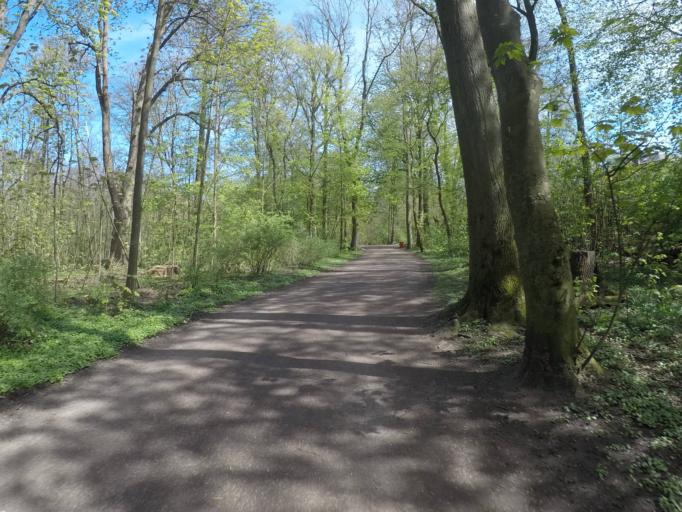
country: DE
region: Hamburg
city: Hummelsbuettel
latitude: 53.6353
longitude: 10.0488
